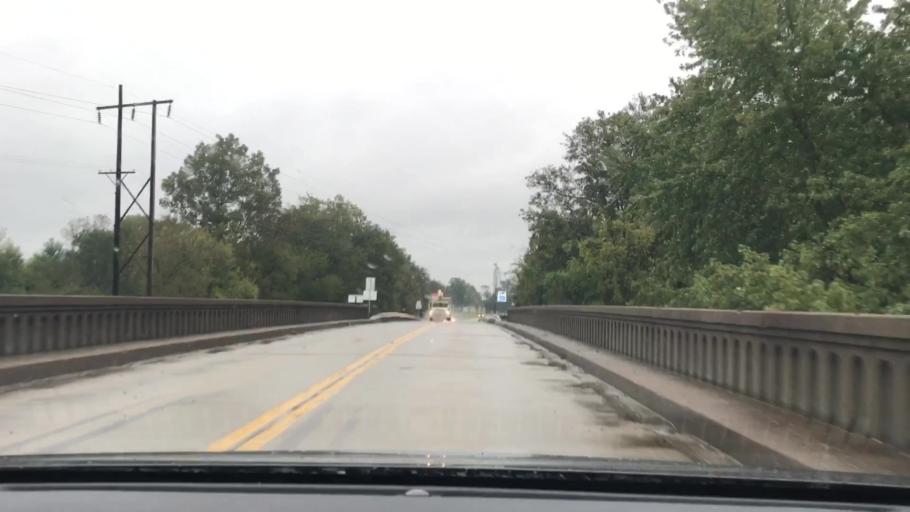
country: US
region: Kentucky
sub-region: McLean County
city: Calhoun
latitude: 37.5266
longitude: -87.3541
